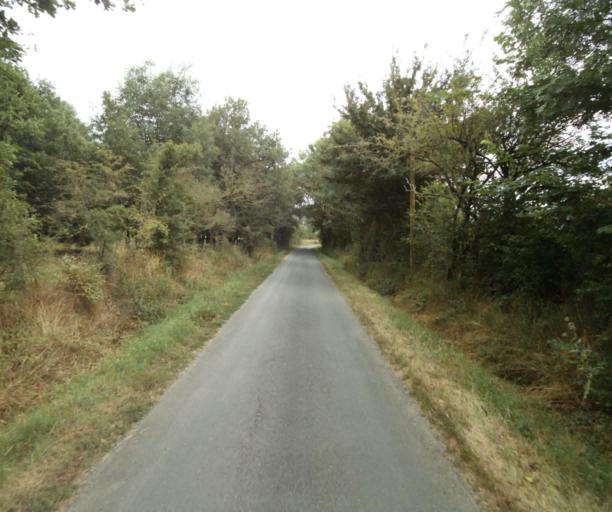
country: FR
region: Midi-Pyrenees
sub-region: Departement du Tarn
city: Soreze
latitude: 43.4637
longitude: 2.0569
